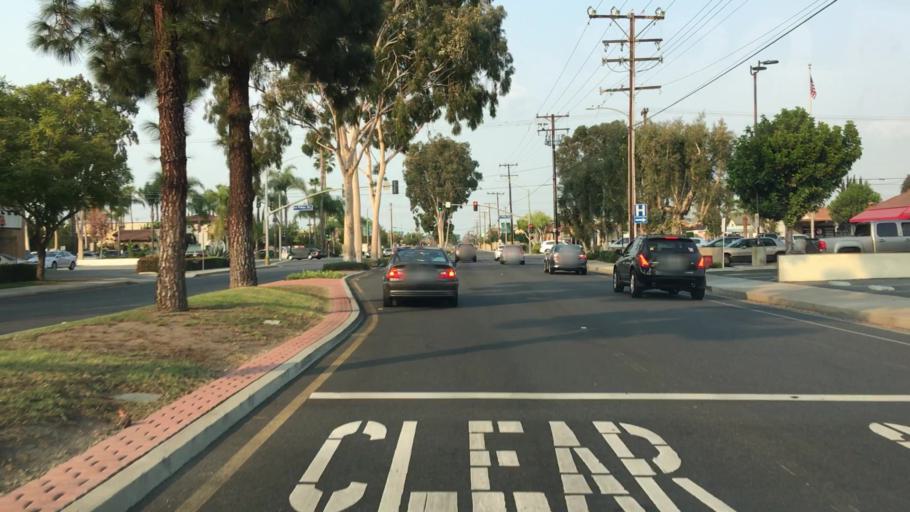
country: US
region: California
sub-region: Orange County
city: La Palma
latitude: 33.8454
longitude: -118.0460
